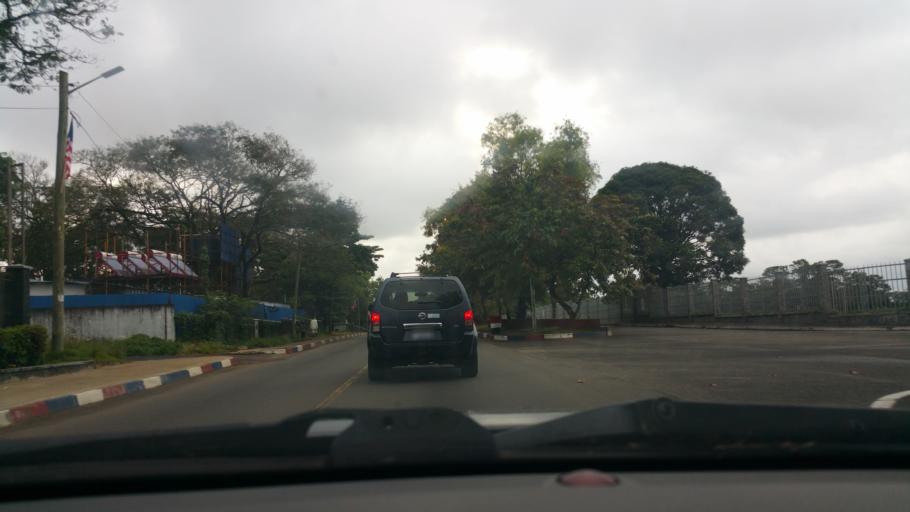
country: LR
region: Montserrado
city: Monrovia
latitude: 6.3018
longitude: -10.7976
